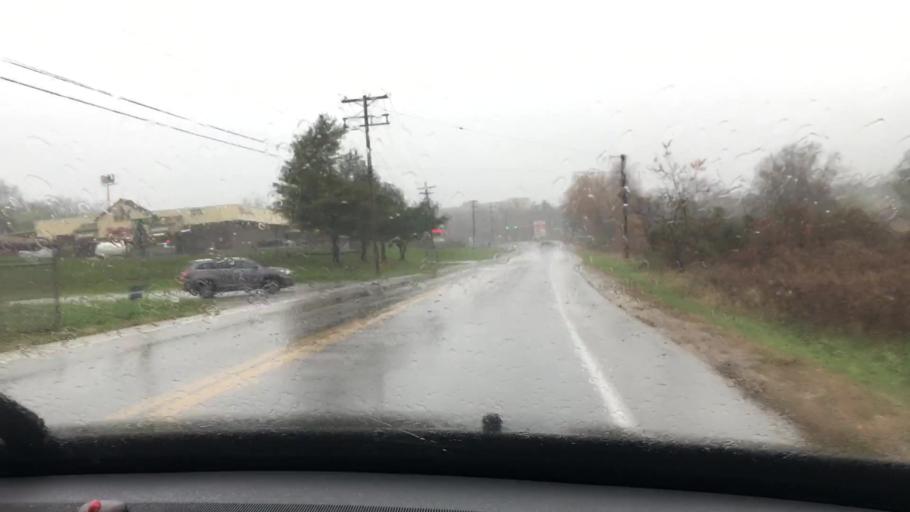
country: US
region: Pennsylvania
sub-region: York County
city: Shrewsbury
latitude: 39.7692
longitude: -76.6608
